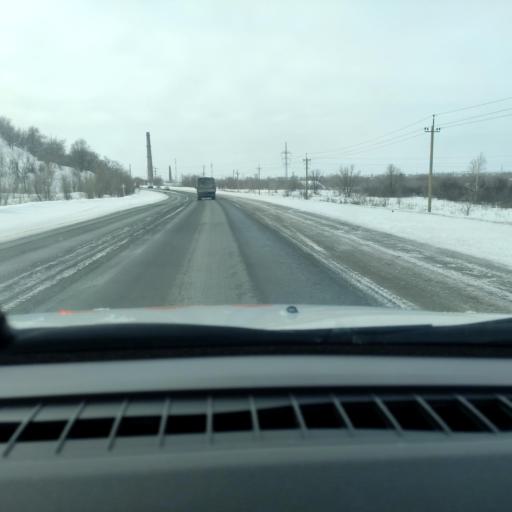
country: RU
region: Samara
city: Chapayevsk
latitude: 52.9323
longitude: 49.7144
